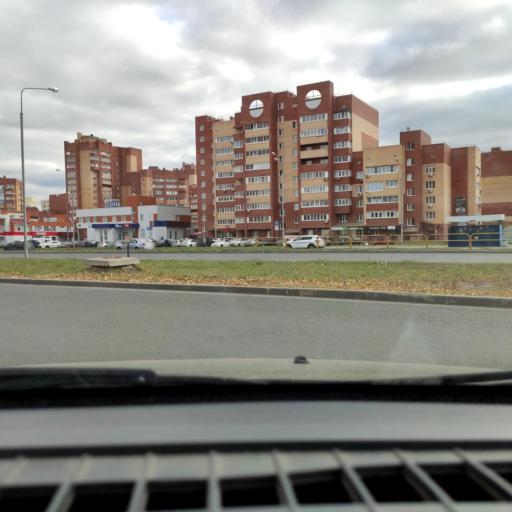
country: RU
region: Samara
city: Tol'yatti
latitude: 53.5363
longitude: 49.3517
